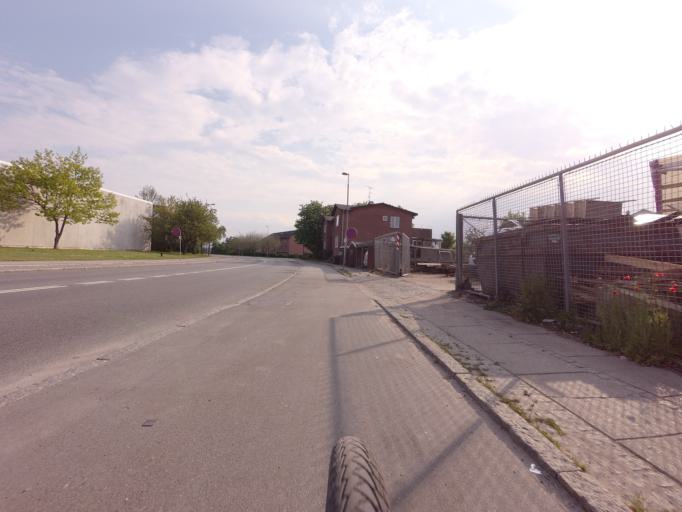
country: DK
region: Capital Region
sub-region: Glostrup Kommune
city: Glostrup
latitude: 55.6693
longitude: 12.4172
